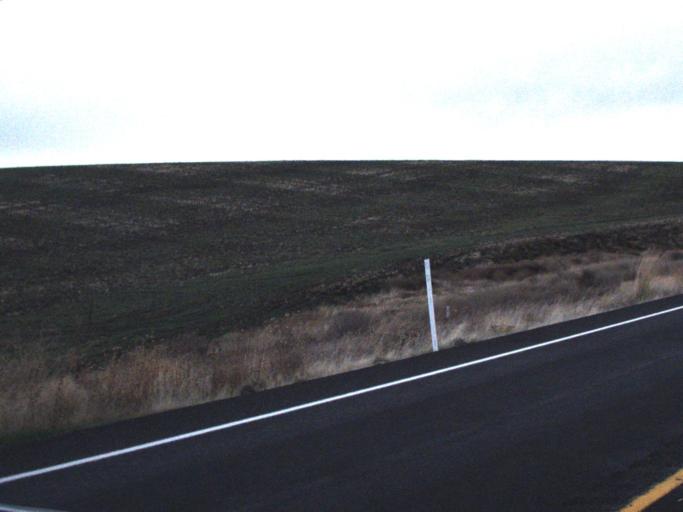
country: US
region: Washington
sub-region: Walla Walla County
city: Waitsburg
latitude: 46.2563
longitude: -118.1513
